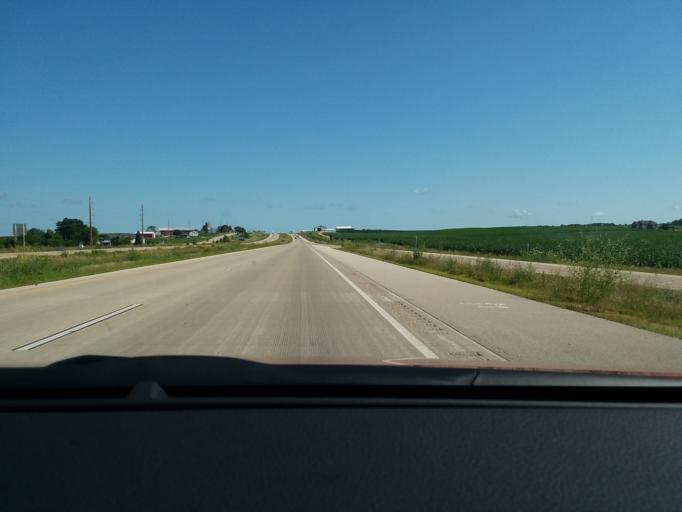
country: US
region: Wisconsin
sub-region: Dane County
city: Windsor
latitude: 43.2195
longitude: -89.3226
